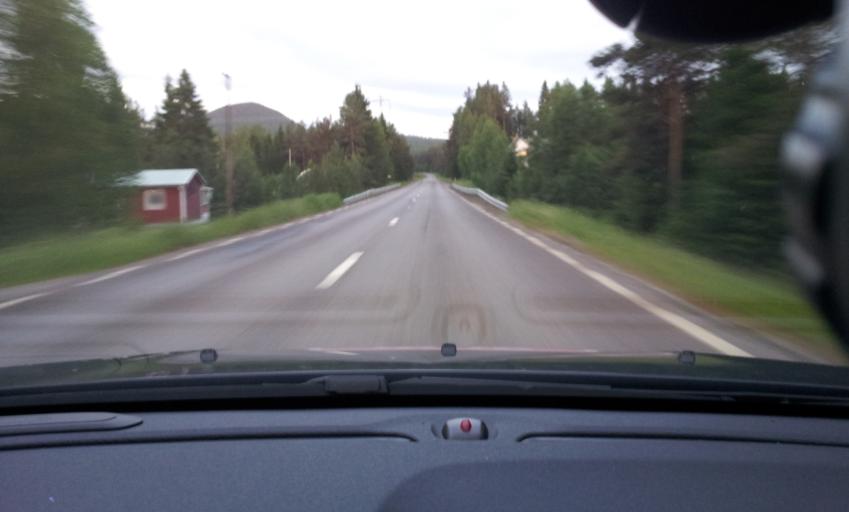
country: SE
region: Jaemtland
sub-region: Ragunda Kommun
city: Hammarstrand
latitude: 63.0703
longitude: 16.3840
